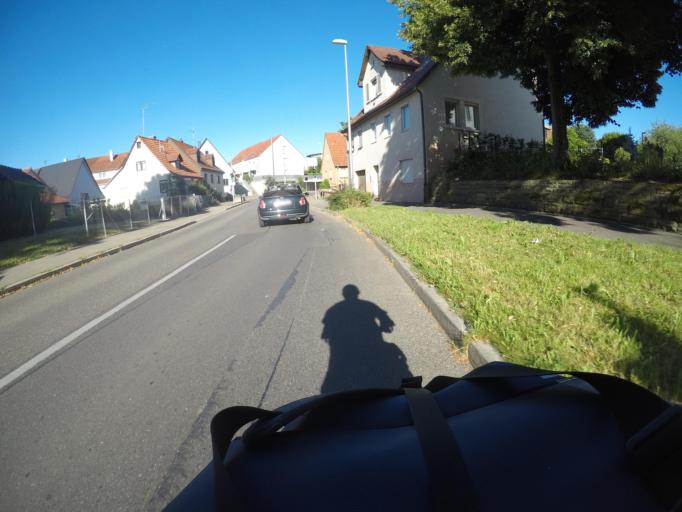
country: DE
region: Baden-Wuerttemberg
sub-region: Regierungsbezirk Stuttgart
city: Ludwigsburg
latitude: 48.8913
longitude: 9.2313
